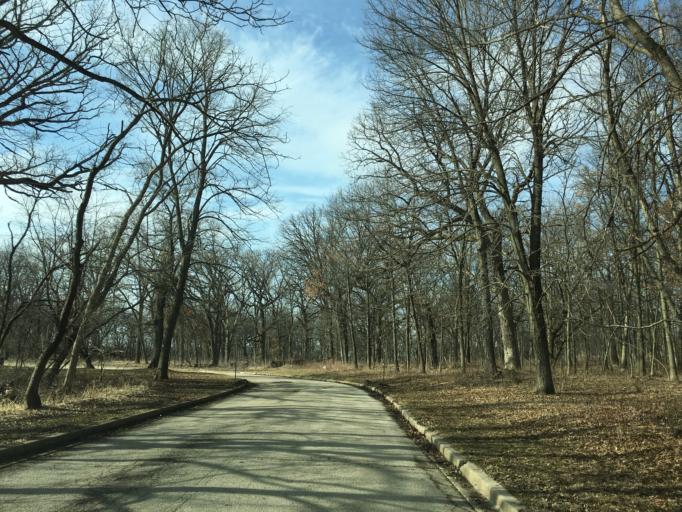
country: US
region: Illinois
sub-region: Cook County
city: Streamwood
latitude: 42.0509
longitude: -88.1969
